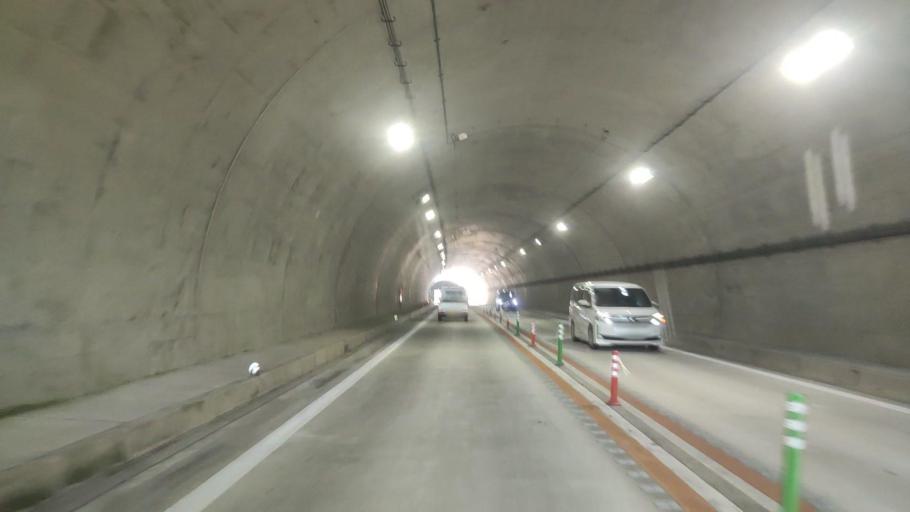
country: JP
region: Wakayama
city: Tanabe
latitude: 33.5827
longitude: 135.4515
